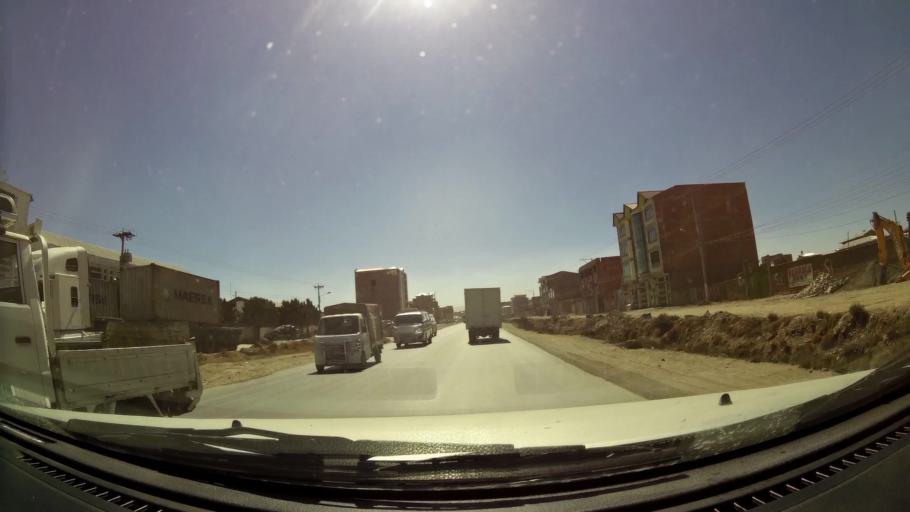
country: BO
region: La Paz
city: La Paz
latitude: -16.5542
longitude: -68.2088
